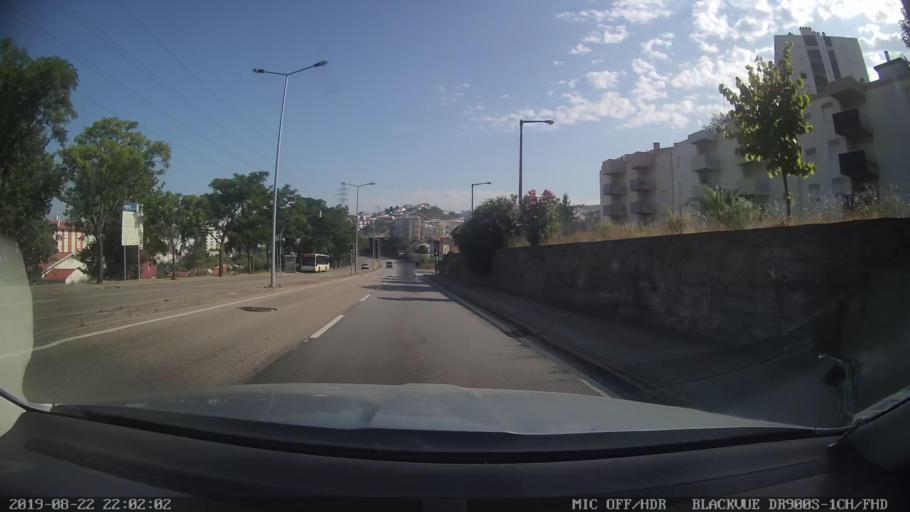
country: PT
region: Coimbra
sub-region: Coimbra
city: Coimbra
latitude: 40.1950
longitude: -8.3980
